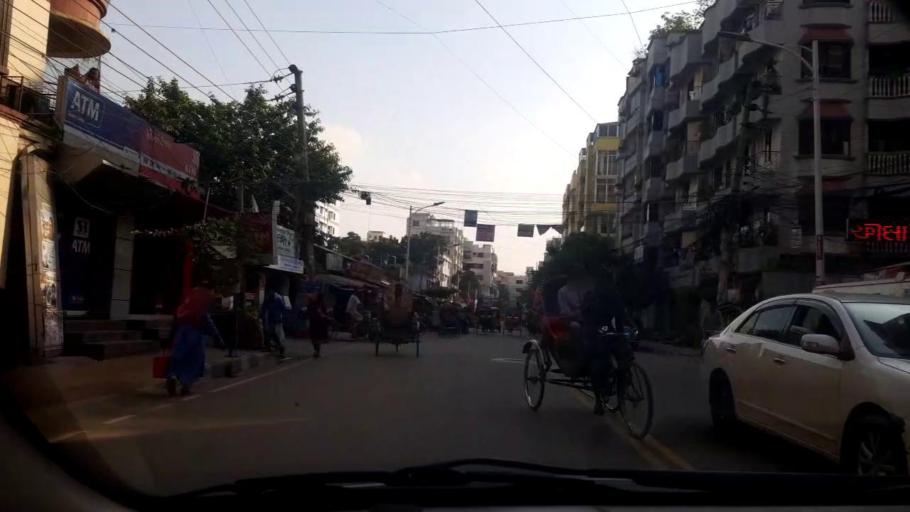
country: BD
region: Dhaka
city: Tungi
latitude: 23.8661
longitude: 90.3887
